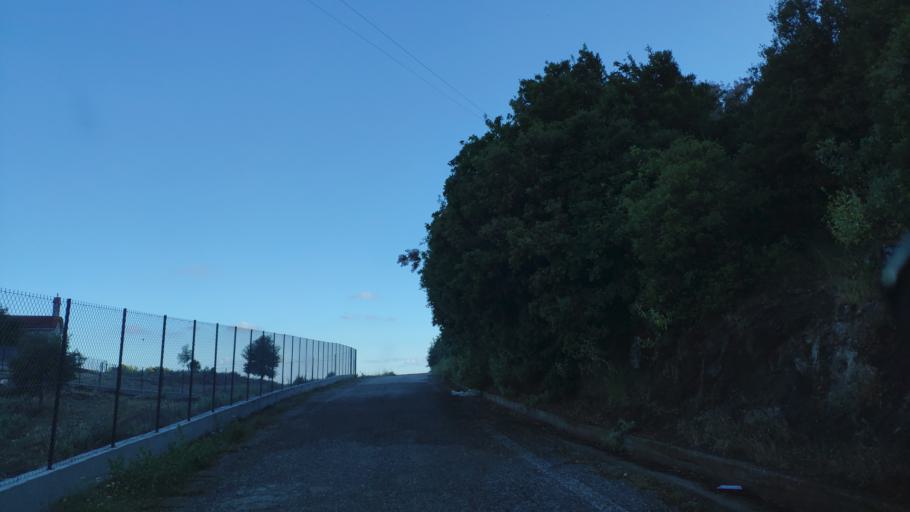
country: GR
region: West Greece
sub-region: Nomos Aitolias kai Akarnanias
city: Fitiai
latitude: 38.6495
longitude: 21.1988
